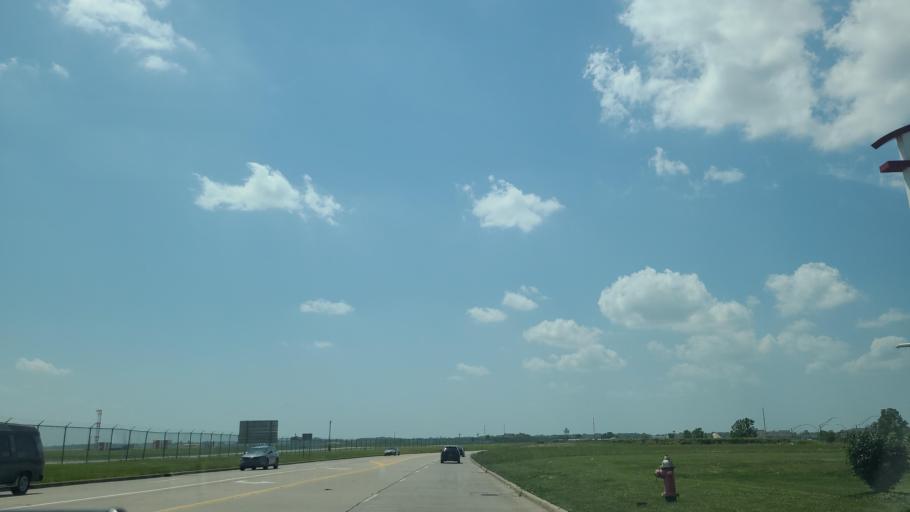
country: US
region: Ohio
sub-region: Cuyahoga County
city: Brook Park
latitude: 41.4187
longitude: -81.8329
